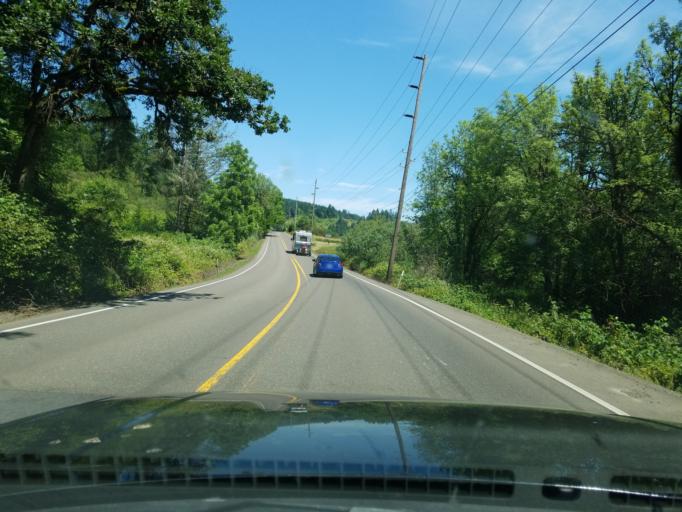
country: US
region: Oregon
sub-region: Yamhill County
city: Yamhill
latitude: 45.3884
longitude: -123.1377
